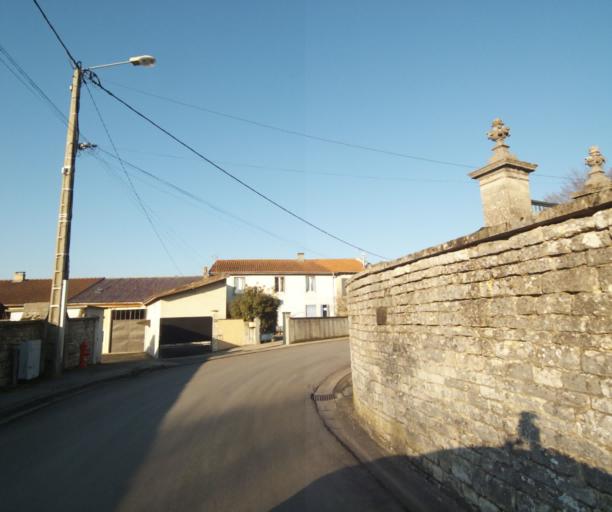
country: FR
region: Champagne-Ardenne
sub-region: Departement de la Haute-Marne
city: Bienville
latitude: 48.5738
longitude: 5.0451
